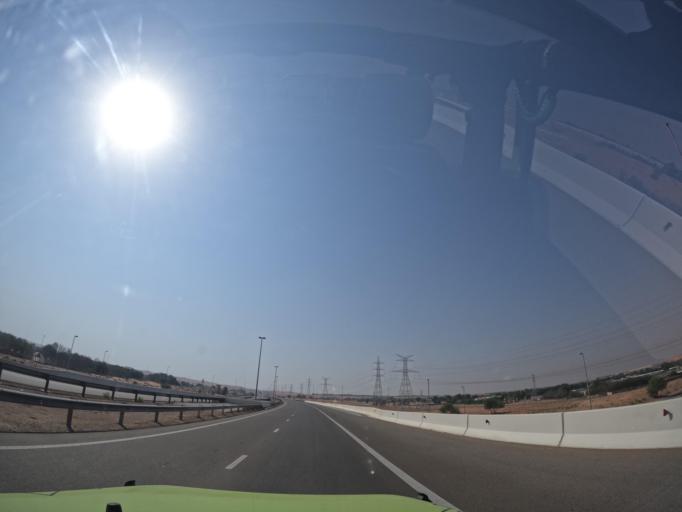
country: OM
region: Al Buraimi
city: Al Buraymi
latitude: 24.3664
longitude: 55.7288
